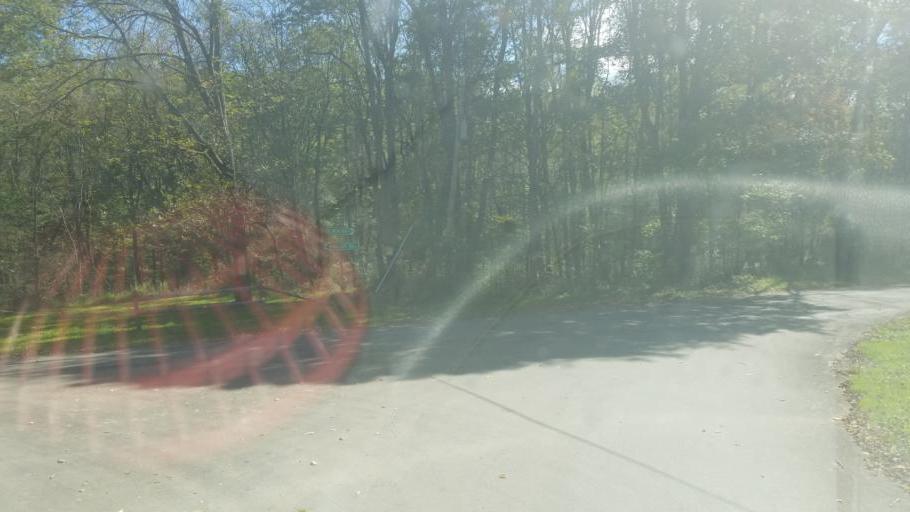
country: US
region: New York
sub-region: Allegany County
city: Cuba
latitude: 42.1687
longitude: -78.3335
